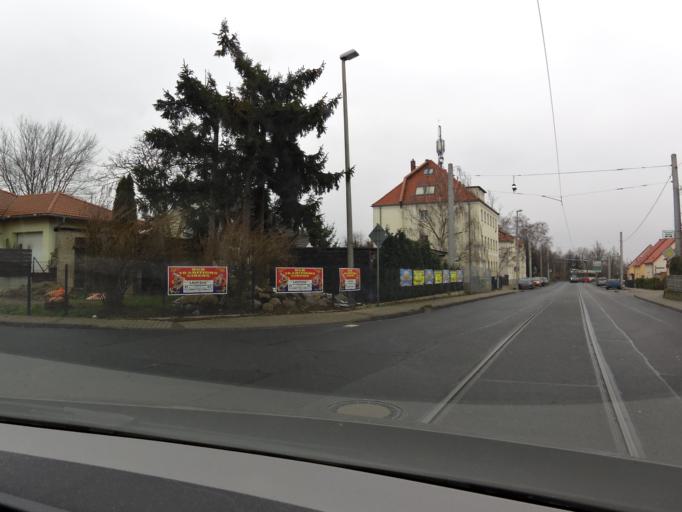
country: DE
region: Saxony
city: Markkleeberg
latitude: 51.2847
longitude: 12.3116
